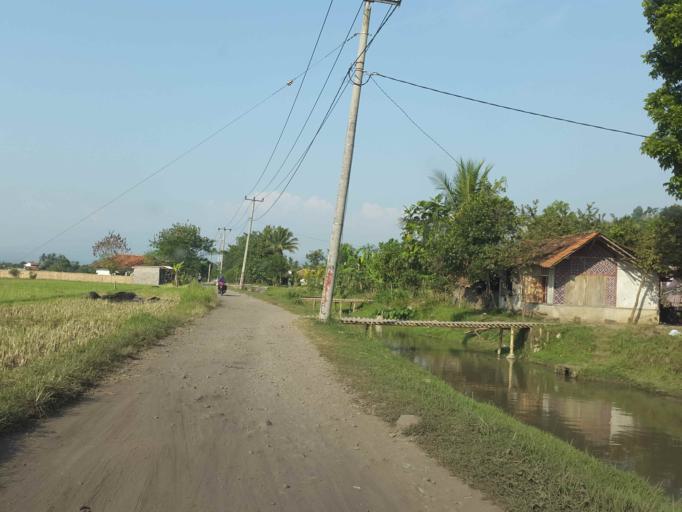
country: ID
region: West Java
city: Ciranjang-hilir
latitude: -6.8508
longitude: 107.2991
